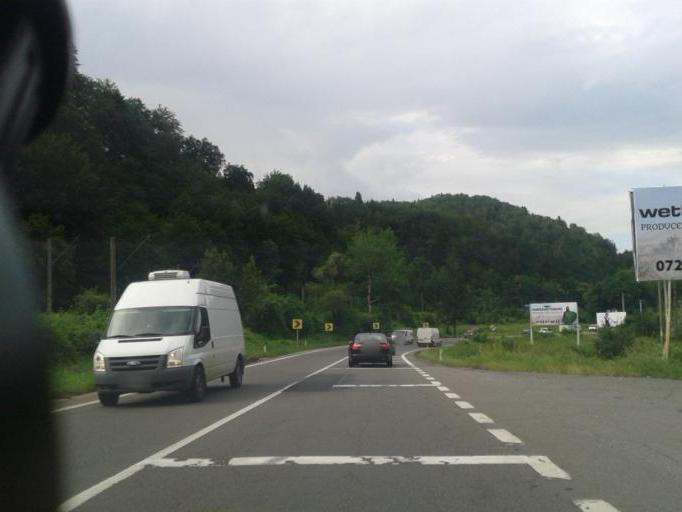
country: RO
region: Brasov
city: Brasov
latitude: 45.5849
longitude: 25.6238
